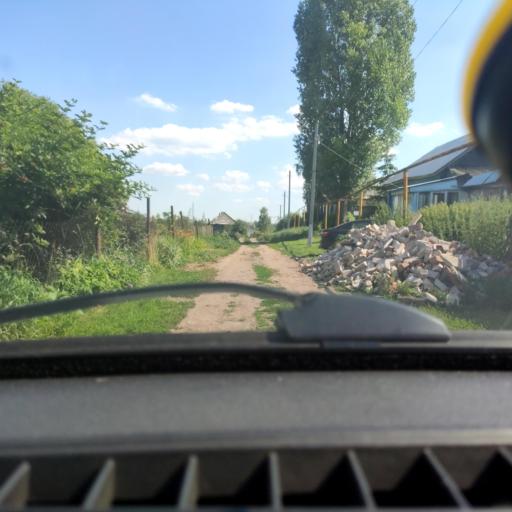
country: RU
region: Samara
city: Povolzhskiy
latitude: 53.7574
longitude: 49.7329
